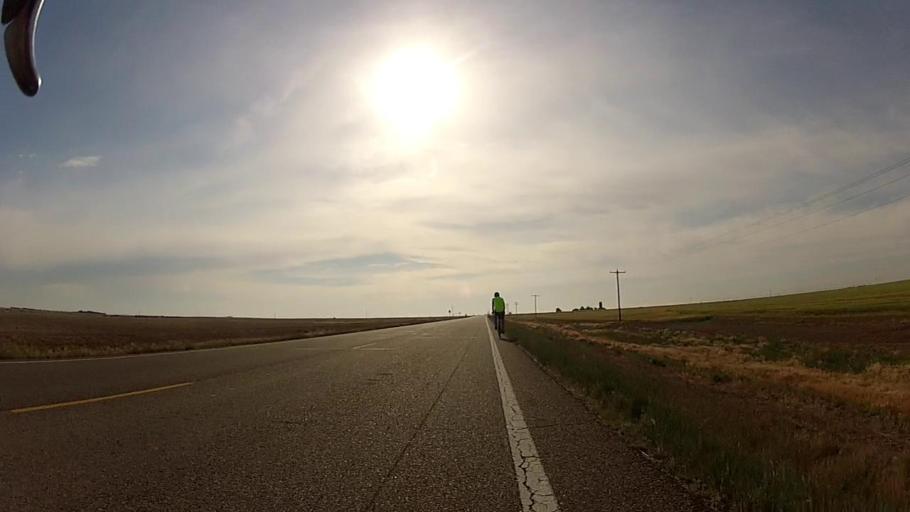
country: US
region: Kansas
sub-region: Grant County
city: Ulysses
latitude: 37.5766
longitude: -101.4577
